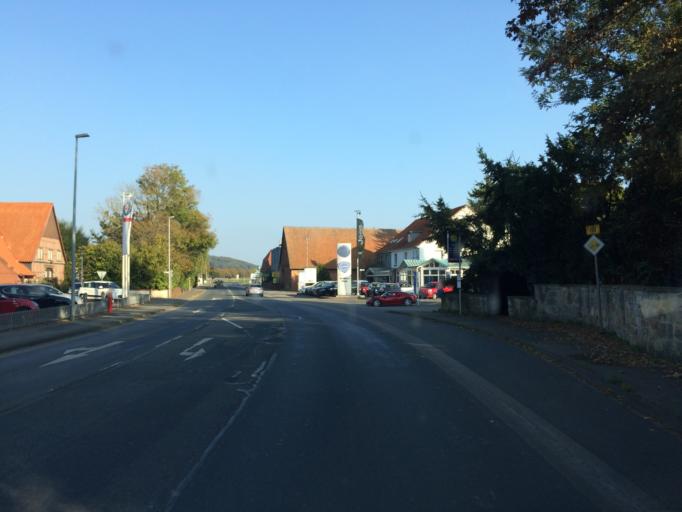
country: DE
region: Lower Saxony
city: Gehrden
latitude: 52.3345
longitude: 9.5817
